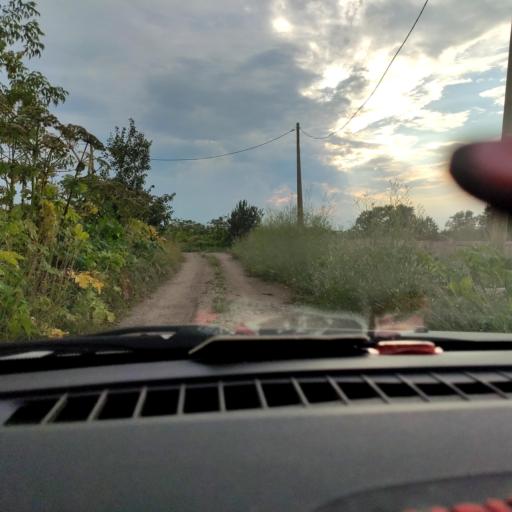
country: RU
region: Perm
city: Kultayevo
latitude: 57.8573
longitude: 55.9749
